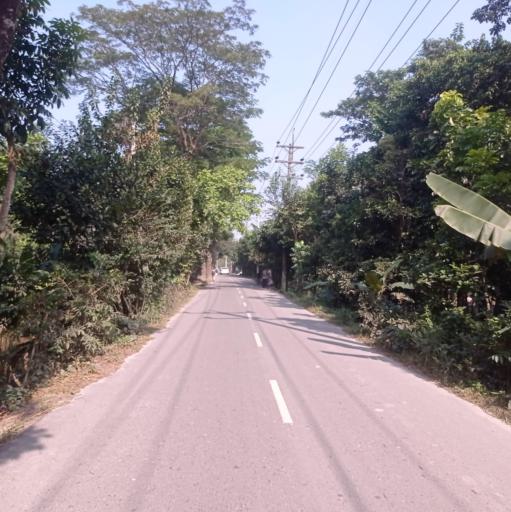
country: BD
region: Dhaka
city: Narsingdi
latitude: 24.0627
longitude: 90.6893
